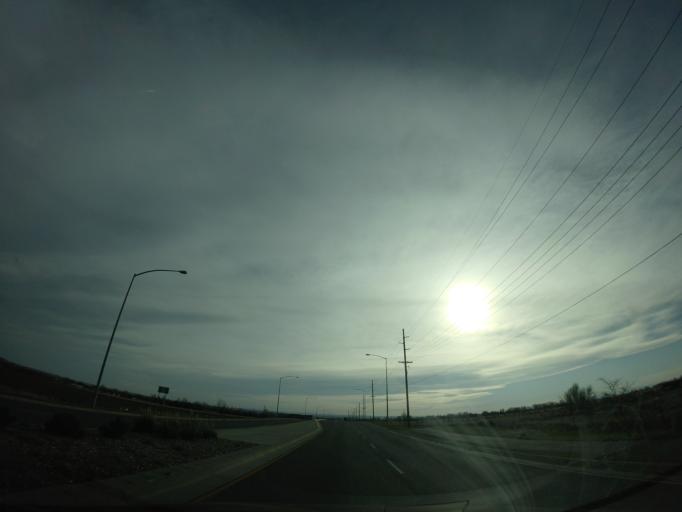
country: US
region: Montana
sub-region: Yellowstone County
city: Billings
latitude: 45.7819
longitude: -108.6177
